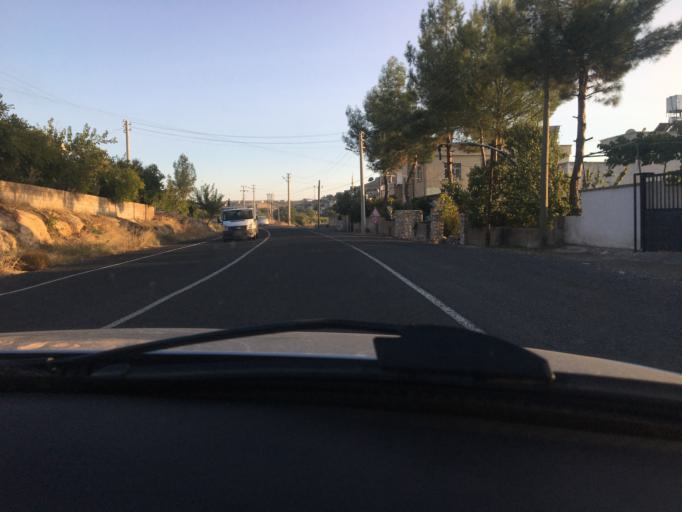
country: TR
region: Sanliurfa
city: Halfeti
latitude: 37.2177
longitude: 37.9545
